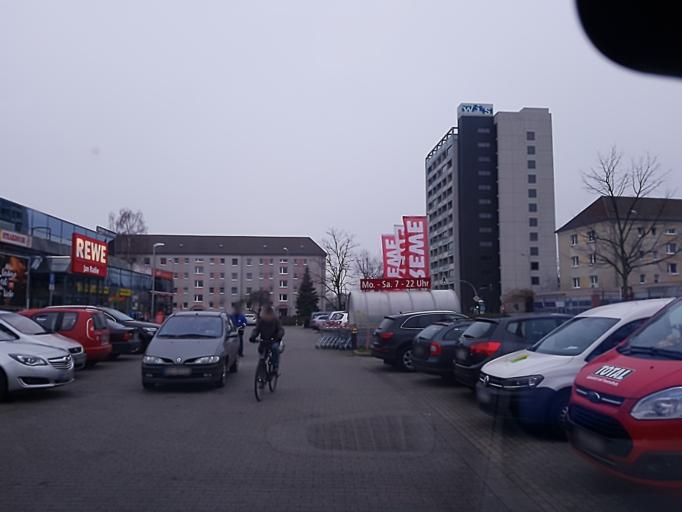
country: DE
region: Brandenburg
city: Lubbenau
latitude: 51.8605
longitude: 13.9526
